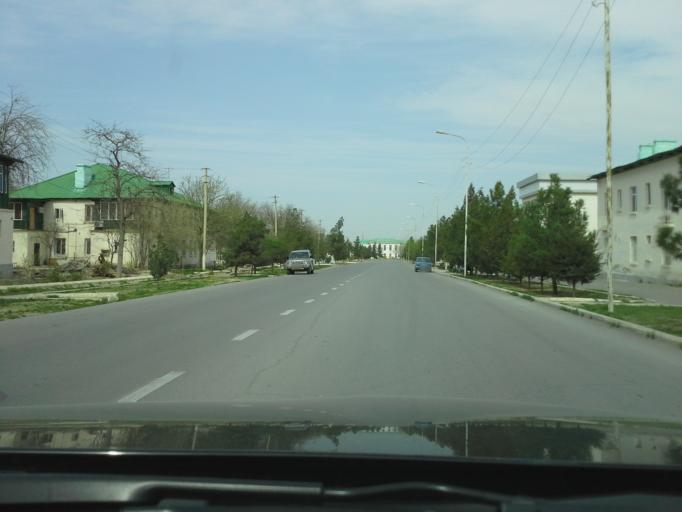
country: TM
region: Ahal
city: Abadan
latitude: 38.0595
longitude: 58.1542
